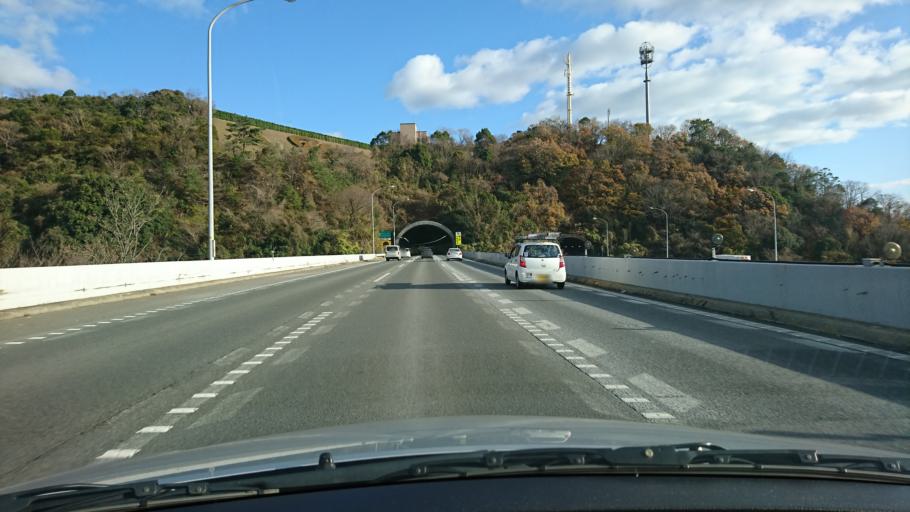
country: JP
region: Hyogo
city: Takarazuka
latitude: 34.8214
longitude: 135.3340
